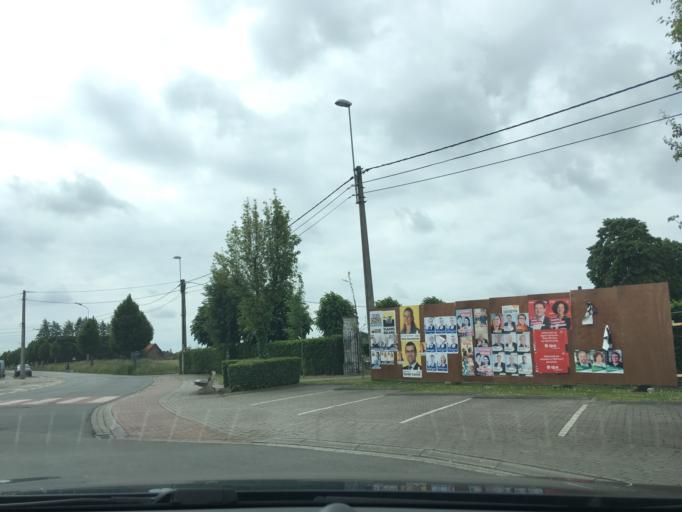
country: BE
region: Flanders
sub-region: Provincie West-Vlaanderen
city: Ledegem
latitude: 50.8492
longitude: 3.0889
